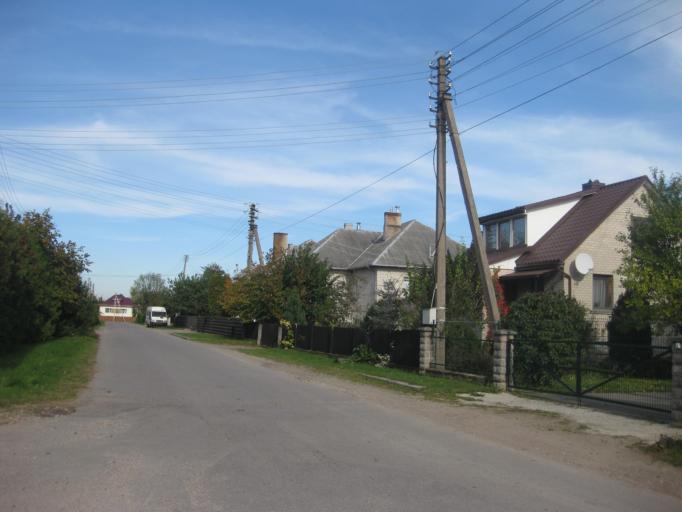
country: LT
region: Kauno apskritis
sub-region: Kauno rajonas
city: Garliava
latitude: 54.8231
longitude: 23.8610
